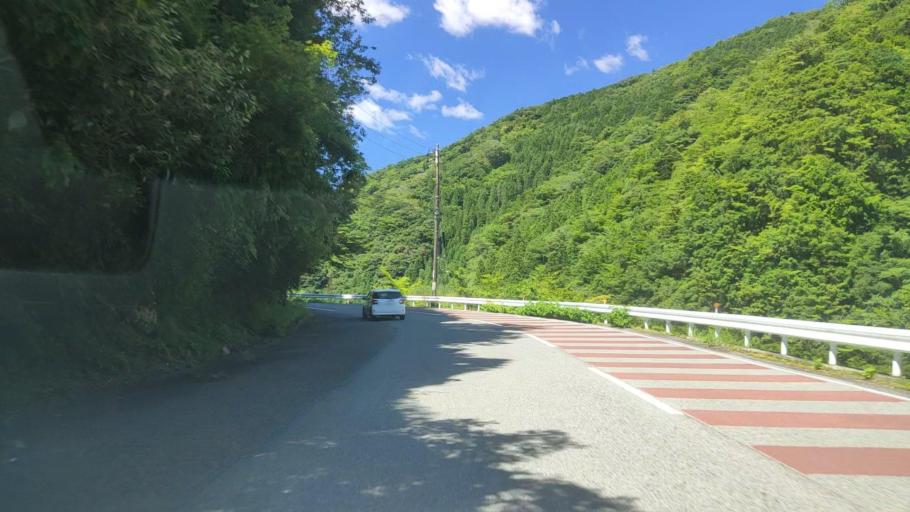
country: JP
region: Mie
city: Owase
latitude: 34.1989
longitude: 135.9993
